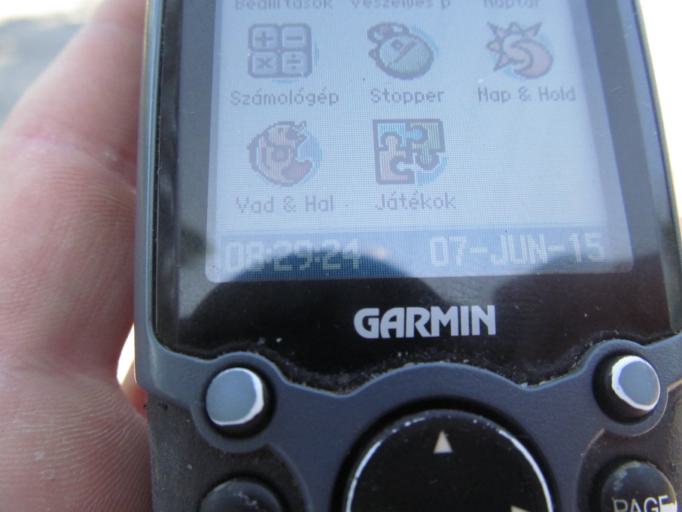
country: HU
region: Pest
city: Pilisszentkereszt
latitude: 47.7188
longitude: 18.8982
